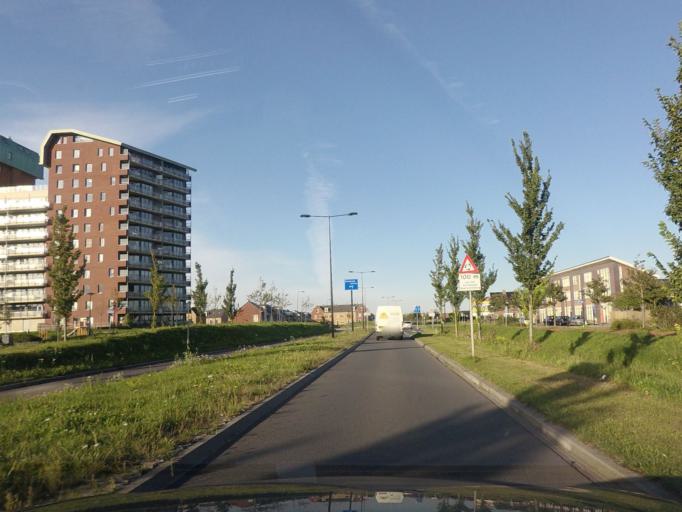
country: NL
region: North Holland
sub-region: Gemeente Beverwijk
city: Beverwijk
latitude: 52.4868
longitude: 4.6795
